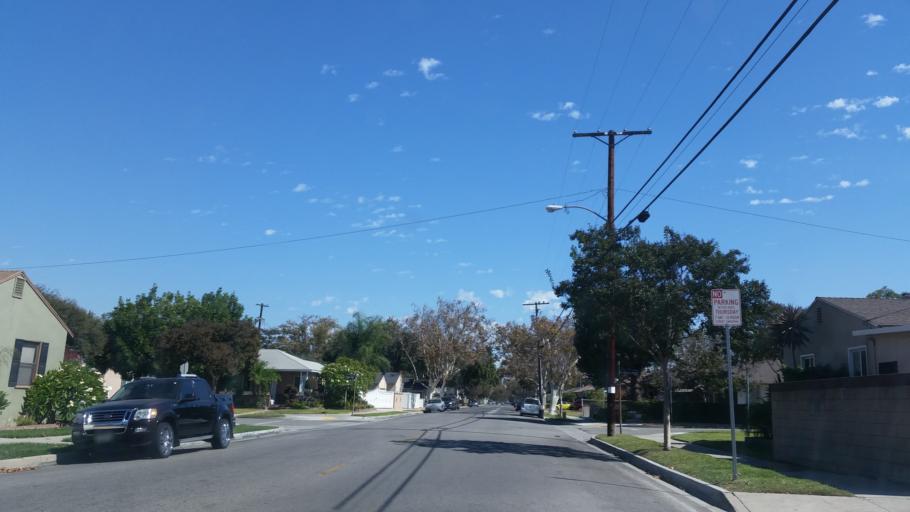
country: US
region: California
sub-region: Los Angeles County
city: Lakewood
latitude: 33.8641
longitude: -118.1423
